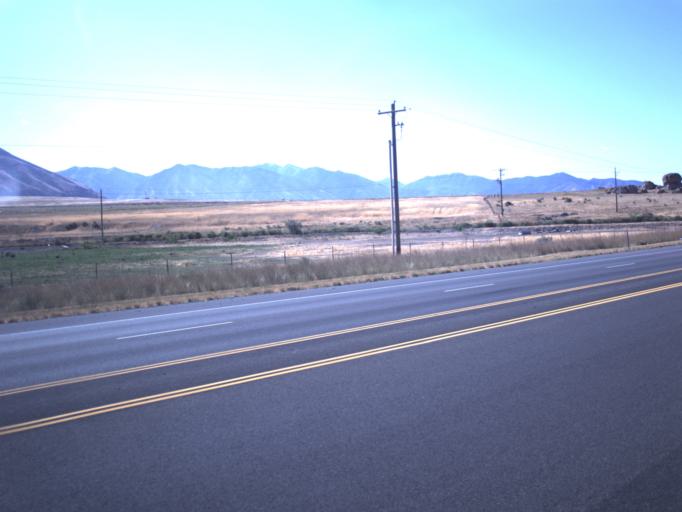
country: US
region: Utah
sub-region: Tooele County
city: Stansbury park
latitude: 40.6647
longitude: -112.2868
